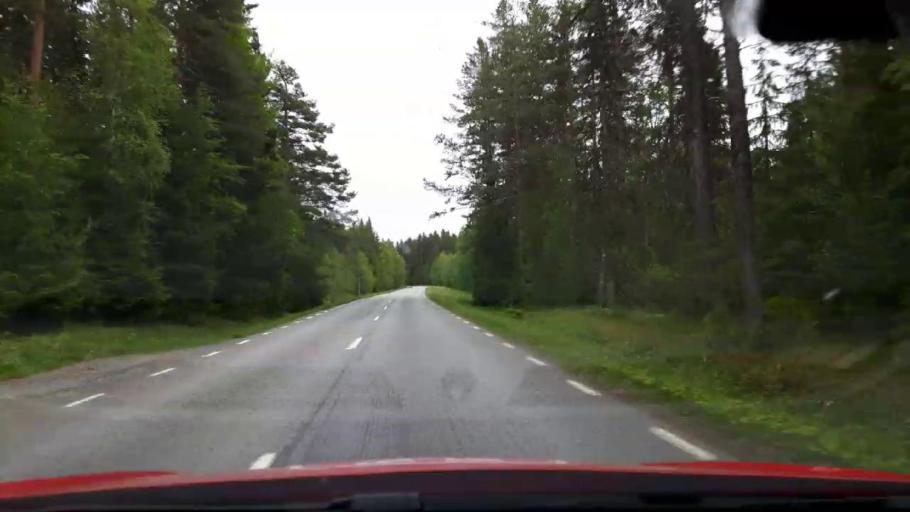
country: SE
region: Jaemtland
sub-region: Stroemsunds Kommun
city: Stroemsund
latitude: 63.4301
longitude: 15.5009
